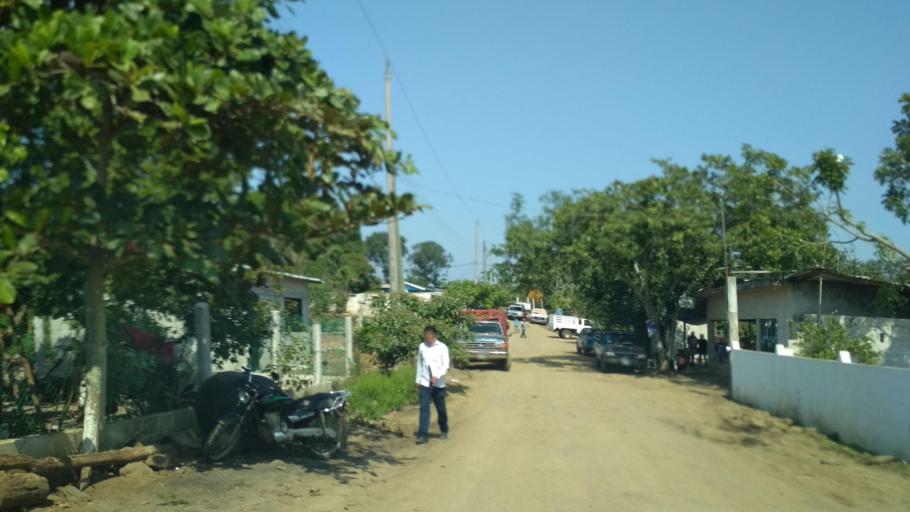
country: MX
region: Puebla
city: San Jose Acateno
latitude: 20.1762
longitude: -97.2335
